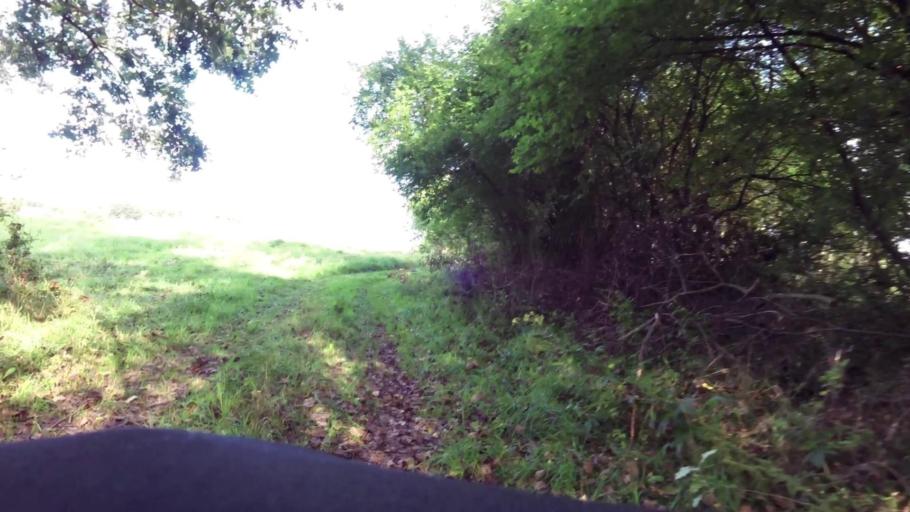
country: PL
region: West Pomeranian Voivodeship
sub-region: Powiat stargardzki
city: Marianowo
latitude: 53.3836
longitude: 15.3018
